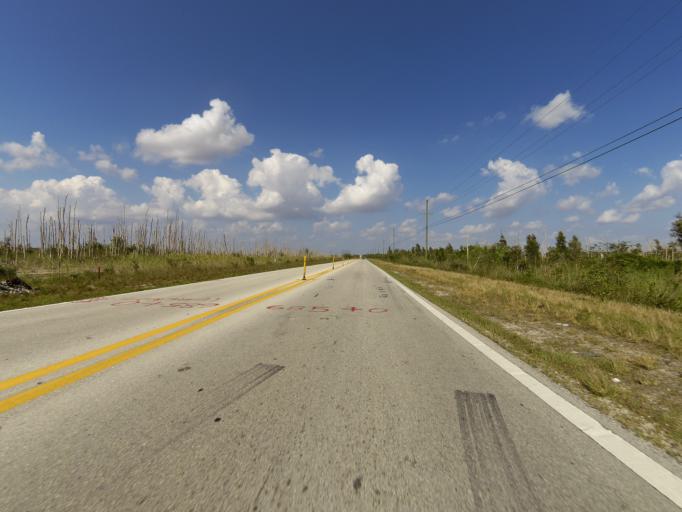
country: US
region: Florida
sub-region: Miami-Dade County
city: Palm Springs North
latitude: 25.9319
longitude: -80.4482
